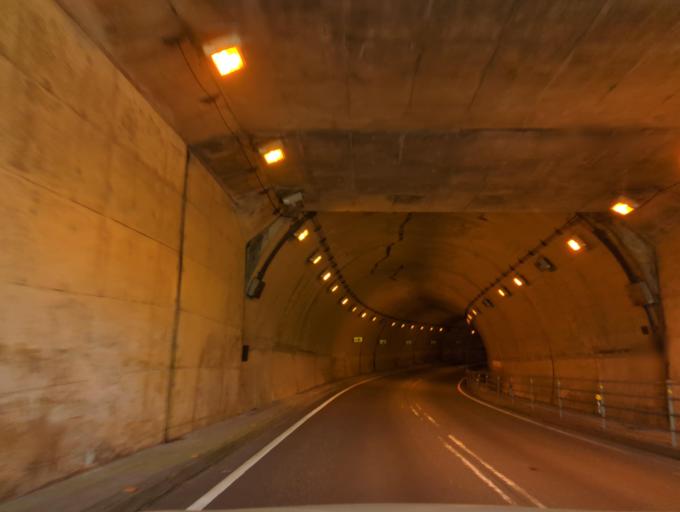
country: JP
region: Niigata
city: Kashiwazaki
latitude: 37.3609
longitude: 138.5315
